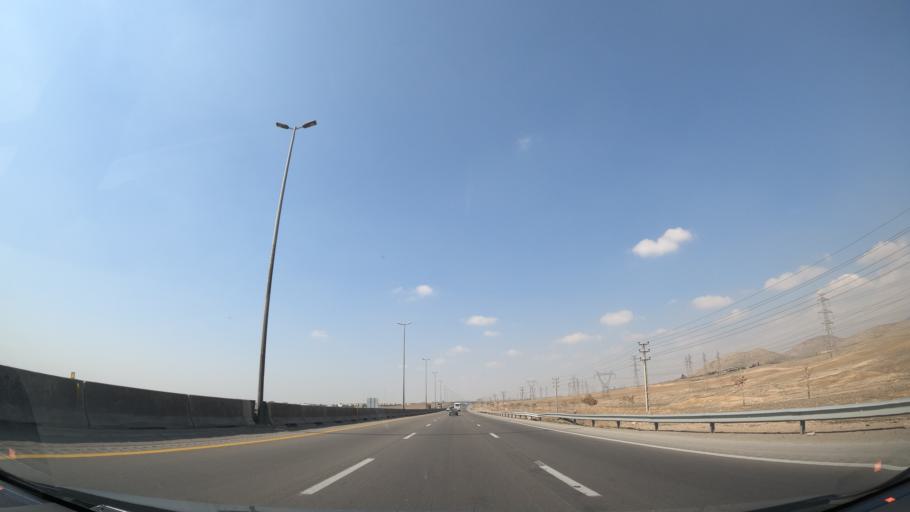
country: IR
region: Qazvin
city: Abyek
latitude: 36.0594
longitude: 50.4998
